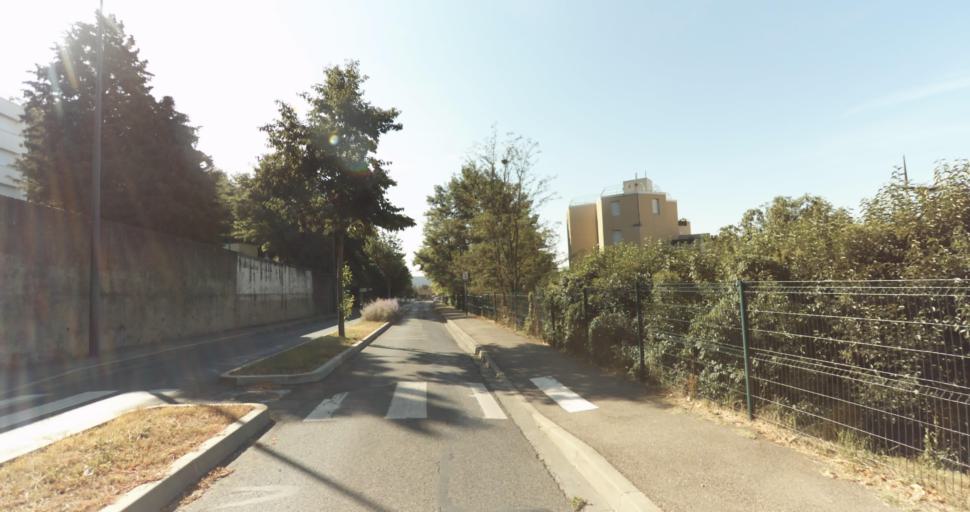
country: FR
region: Rhone-Alpes
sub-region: Departement du Rhone
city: Genay
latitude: 45.8874
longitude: 4.8358
